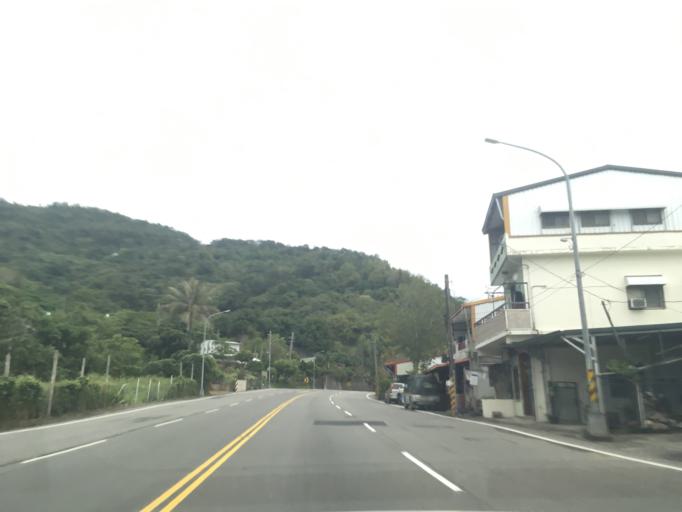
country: TW
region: Taiwan
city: Taitung City
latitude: 22.7484
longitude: 121.0556
